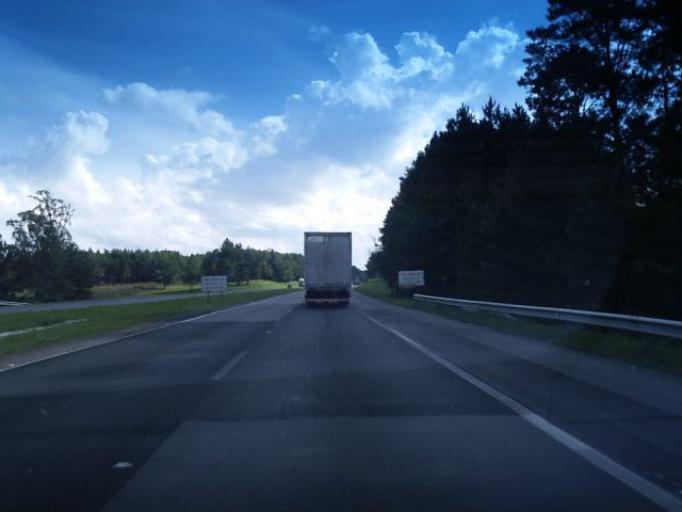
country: BR
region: Parana
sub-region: Piraquara
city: Piraquara
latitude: -25.4043
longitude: -49.0598
